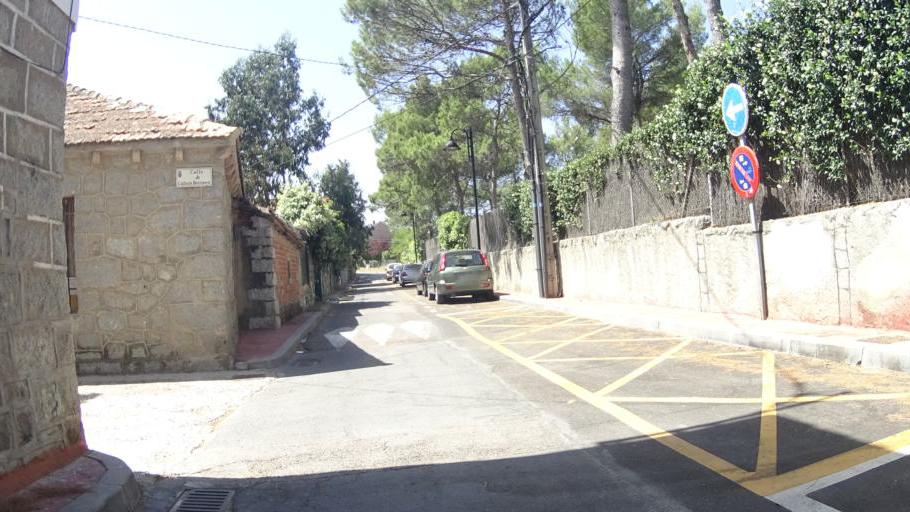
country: ES
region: Madrid
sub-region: Provincia de Madrid
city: Galapagar
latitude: 40.5731
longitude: -4.0078
